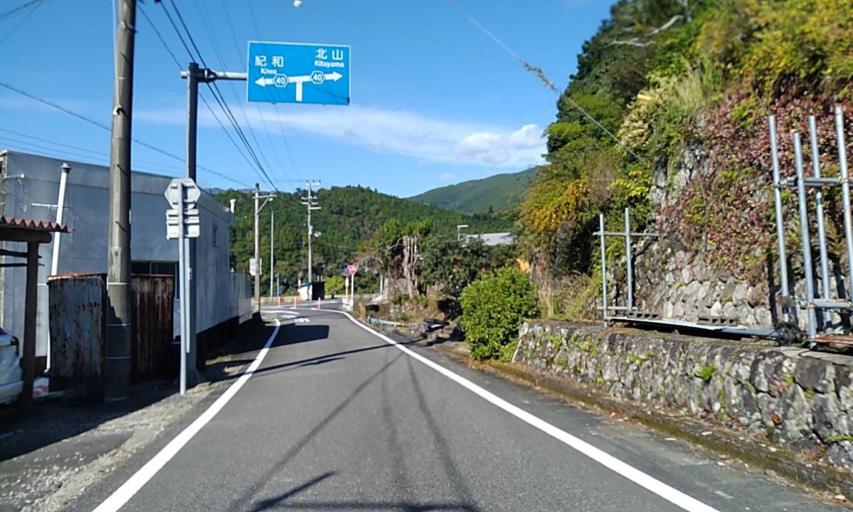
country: JP
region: Wakayama
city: Shingu
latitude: 33.9274
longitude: 135.9809
